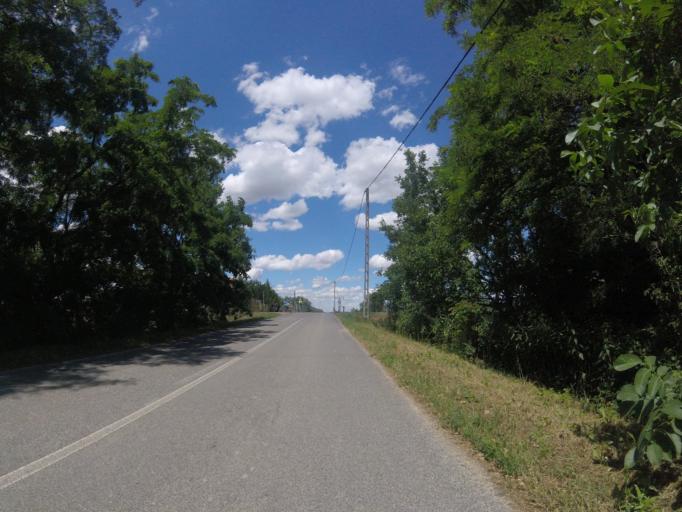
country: HU
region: Tolna
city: Bogyiszlo
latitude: 46.4274
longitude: 18.8944
